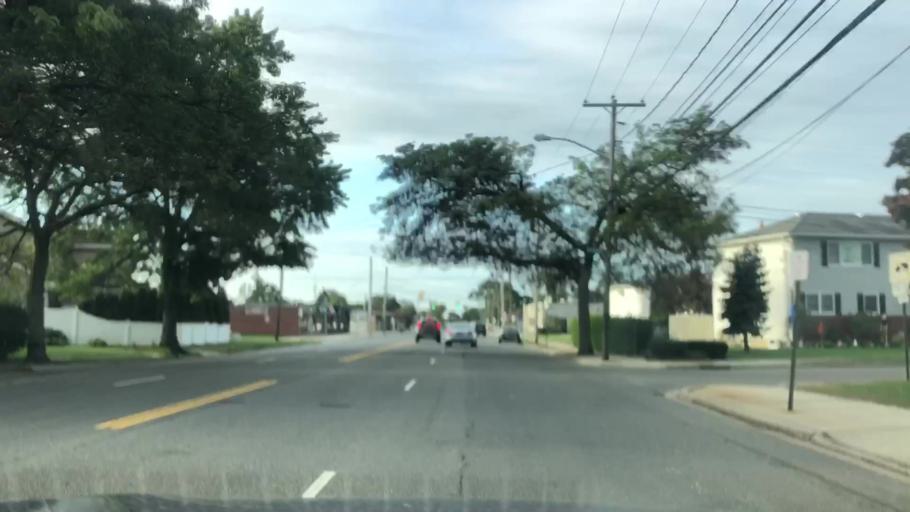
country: US
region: New York
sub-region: Nassau County
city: North Massapequa
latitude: 40.6967
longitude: -73.4638
